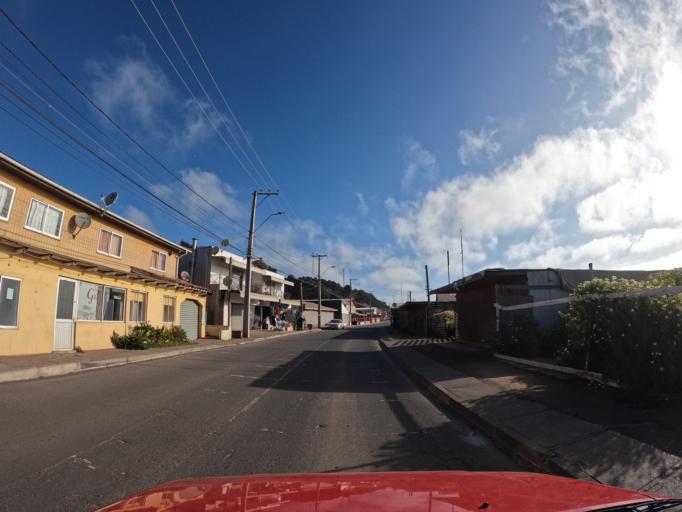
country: CL
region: Maule
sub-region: Provincia de Talca
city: Constitucion
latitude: -34.9362
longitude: -72.1812
